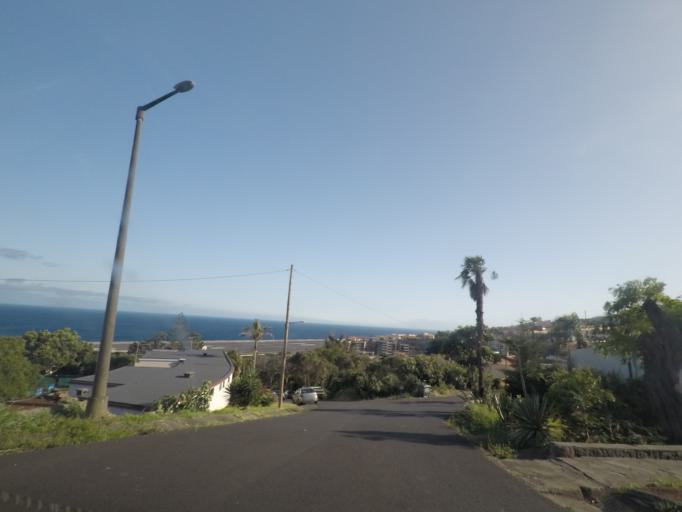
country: PT
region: Madeira
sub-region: Machico
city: Machico
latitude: 32.7098
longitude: -16.7670
